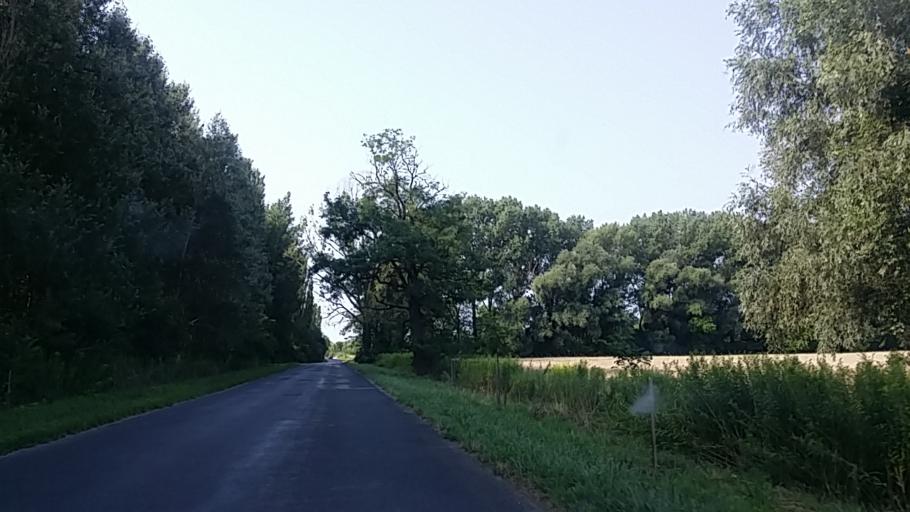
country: HU
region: Veszprem
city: Badacsonytomaj
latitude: 46.8242
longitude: 17.4805
